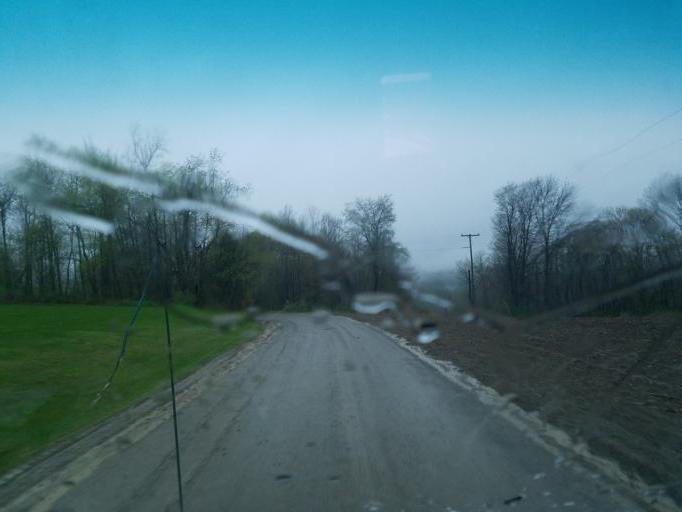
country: US
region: Pennsylvania
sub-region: Tioga County
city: Westfield
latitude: 41.9220
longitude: -77.7215
